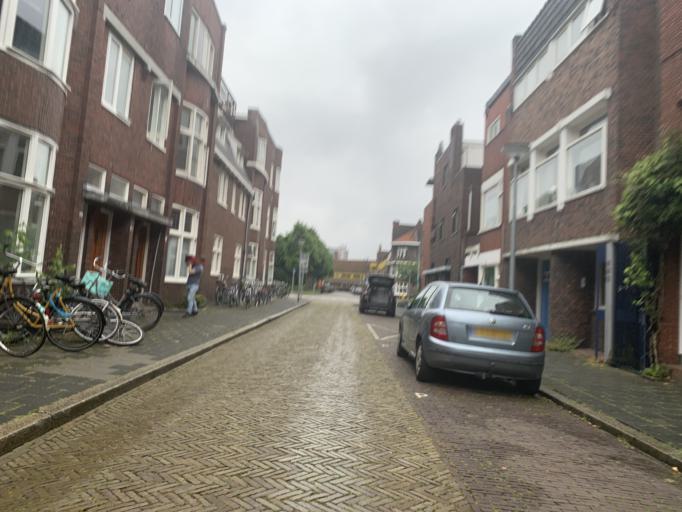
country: NL
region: Groningen
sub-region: Gemeente Groningen
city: Korrewegwijk
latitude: 53.2292
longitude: 6.5648
